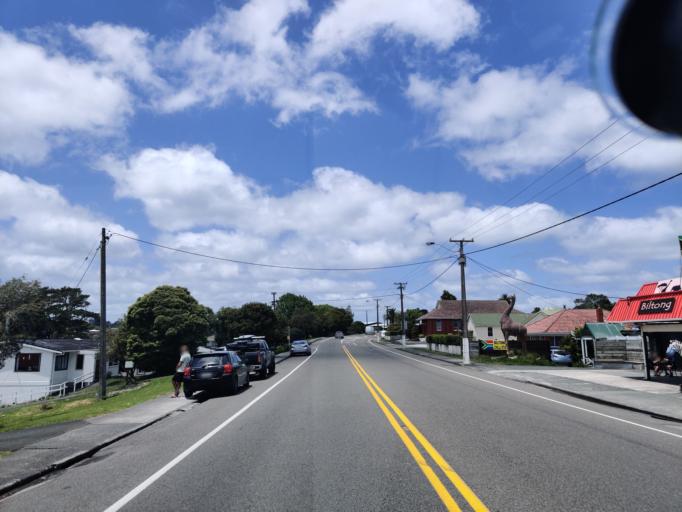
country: NZ
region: Auckland
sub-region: Auckland
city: Wellsford
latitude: -36.2896
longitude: 174.5229
